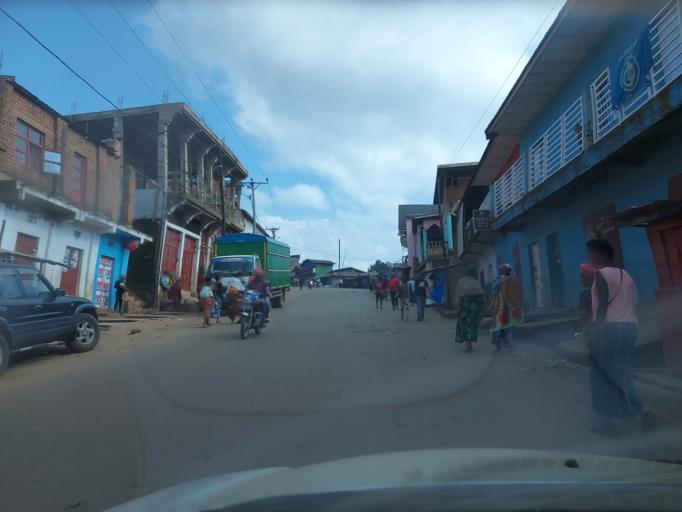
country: CD
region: South Kivu
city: Bukavu
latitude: -2.5205
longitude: 28.8516
